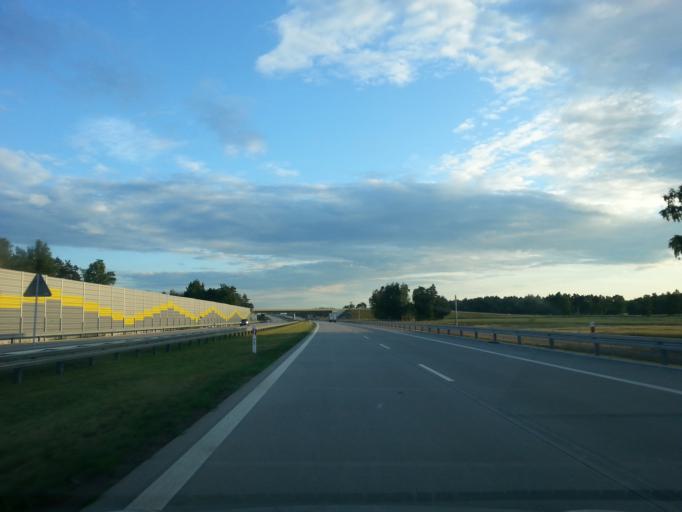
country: PL
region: Lodz Voivodeship
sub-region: Powiat sieradzki
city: Zloczew
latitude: 51.3821
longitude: 18.5530
